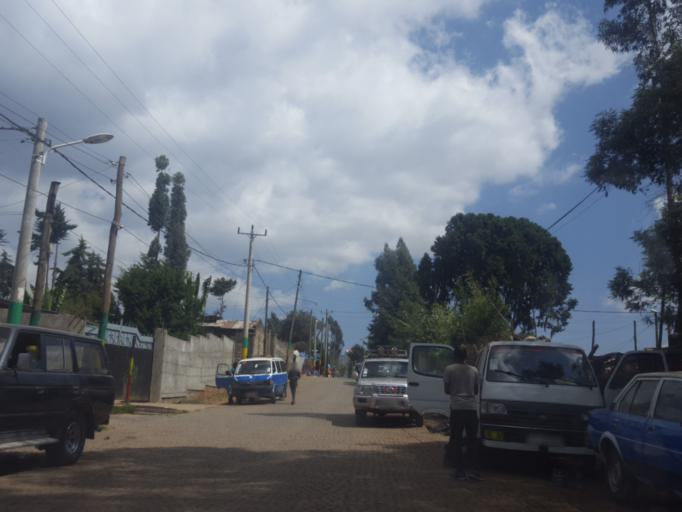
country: ET
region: Adis Abeba
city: Addis Ababa
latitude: 9.0544
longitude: 38.7262
